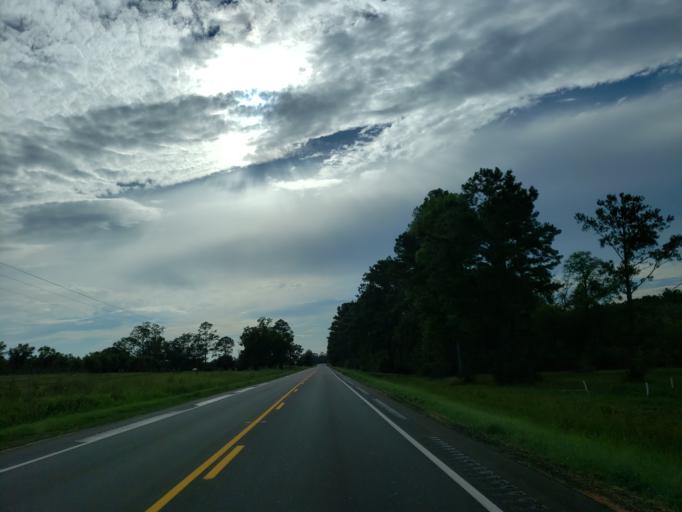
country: US
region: Georgia
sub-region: Irwin County
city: Ocilla
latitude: 31.5633
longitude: -83.3295
